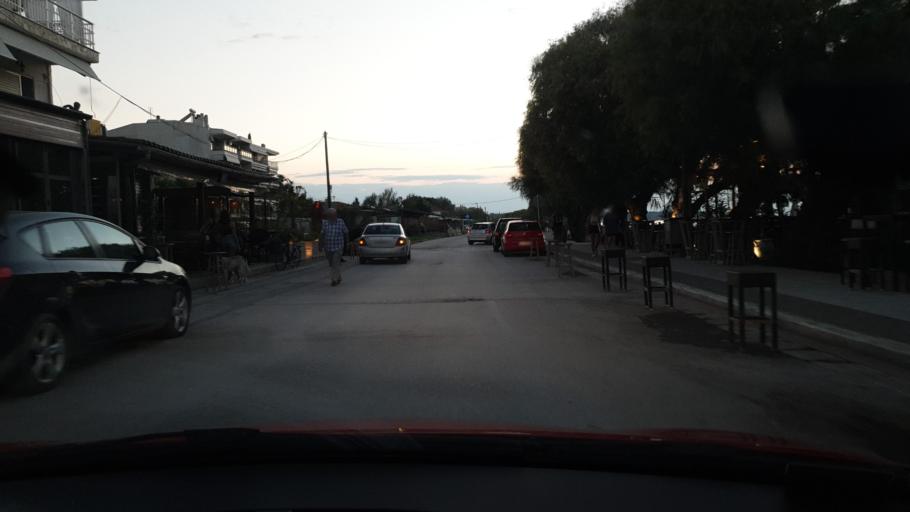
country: GR
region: Central Macedonia
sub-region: Nomos Thessalonikis
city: Neoi Epivates
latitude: 40.5041
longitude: 22.9048
